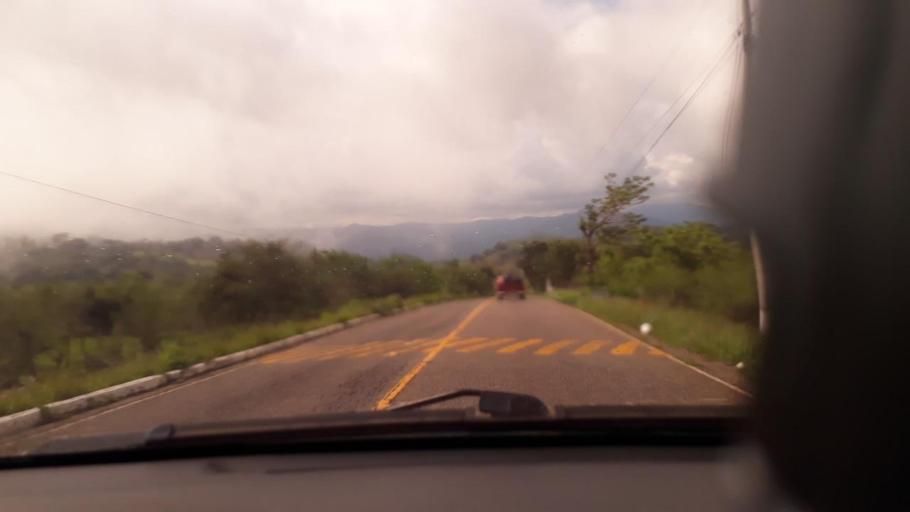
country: GT
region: Jutiapa
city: Jalpatagua
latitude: 14.2053
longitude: -90.0246
